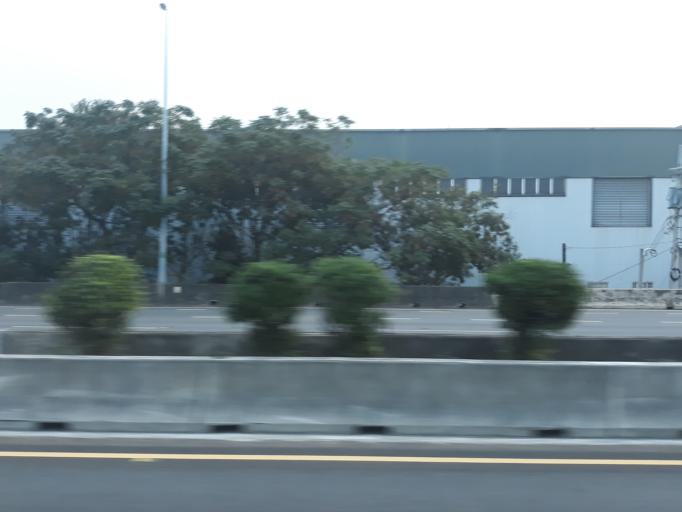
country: TW
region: Taiwan
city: Fengyuan
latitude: 24.2756
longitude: 120.6934
